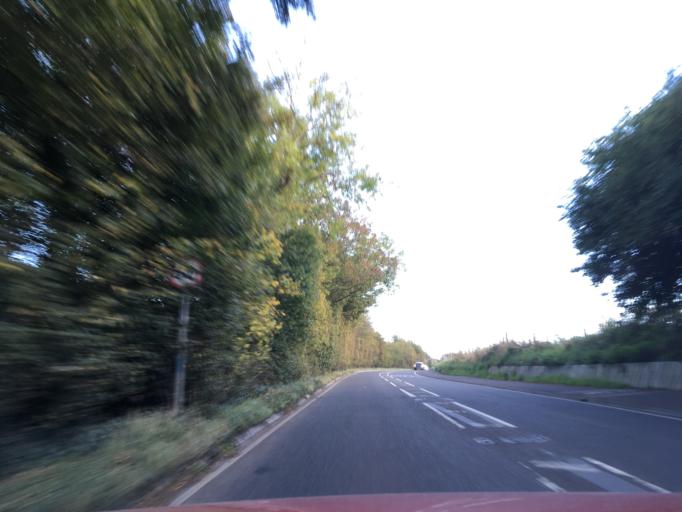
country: GB
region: England
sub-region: North Somerset
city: Easton-in-Gordano
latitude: 51.4662
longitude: -2.6709
